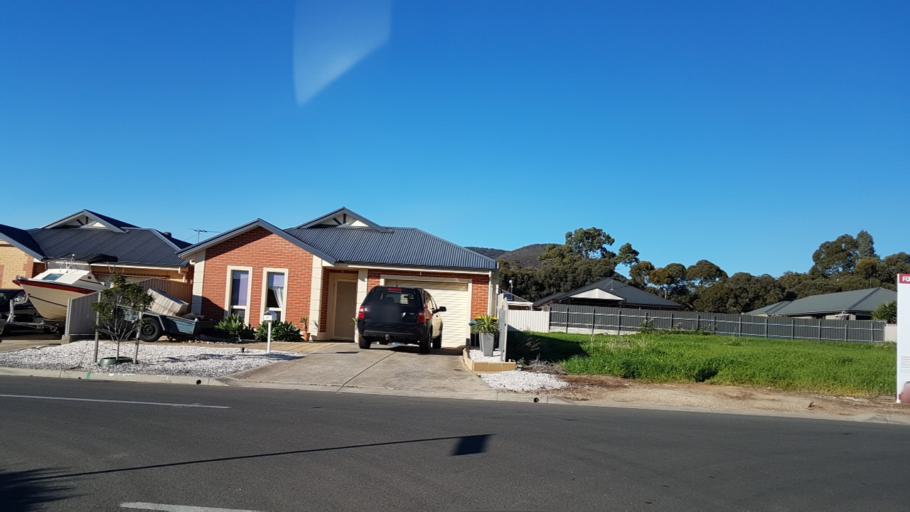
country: AU
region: South Australia
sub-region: Campbelltown
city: Athelstone
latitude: -34.8834
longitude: 138.6859
